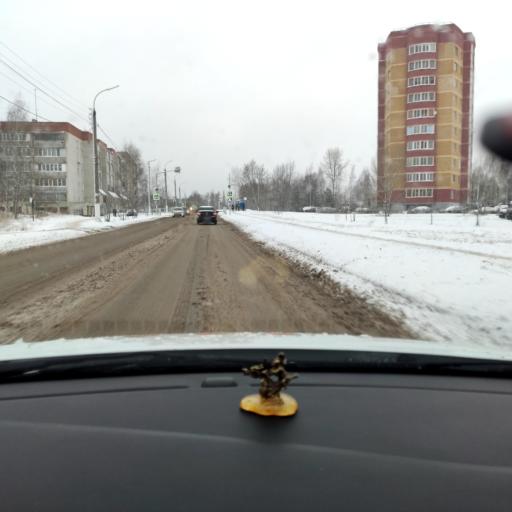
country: RU
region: Tatarstan
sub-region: Zelenodol'skiy Rayon
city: Zelenodolsk
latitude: 55.8596
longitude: 48.5559
